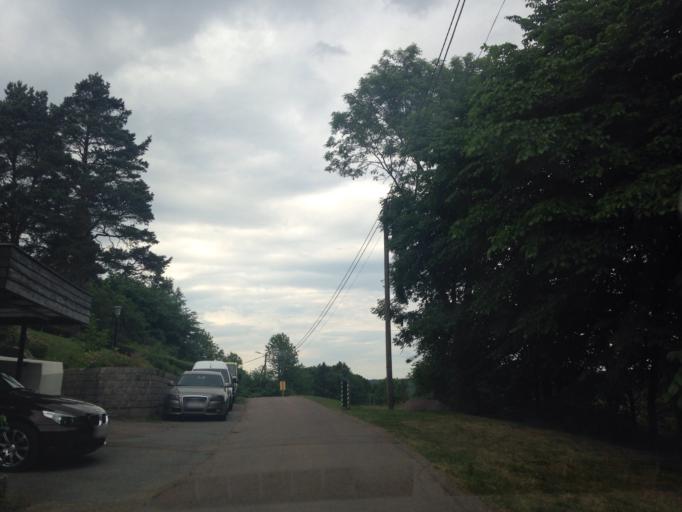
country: SE
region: Vaestra Goetaland
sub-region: Goteborg
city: Goeteborg
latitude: 57.7817
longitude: 11.9319
